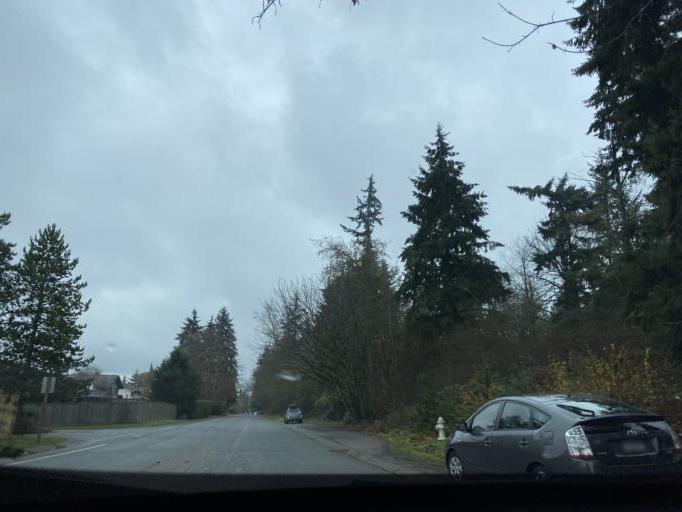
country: US
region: Washington
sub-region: King County
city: Mercer Island
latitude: 47.5431
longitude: -122.2270
